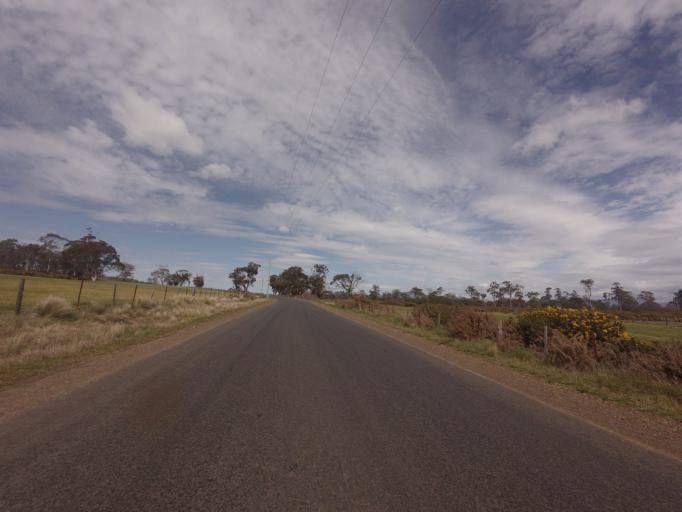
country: AU
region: Tasmania
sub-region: Northern Midlands
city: Longford
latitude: -41.7271
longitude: 147.1925
